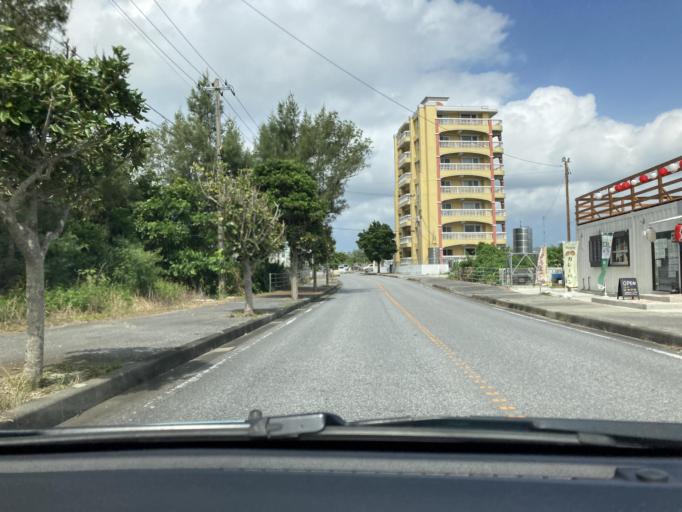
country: JP
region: Okinawa
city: Ishikawa
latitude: 26.4066
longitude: 127.8380
